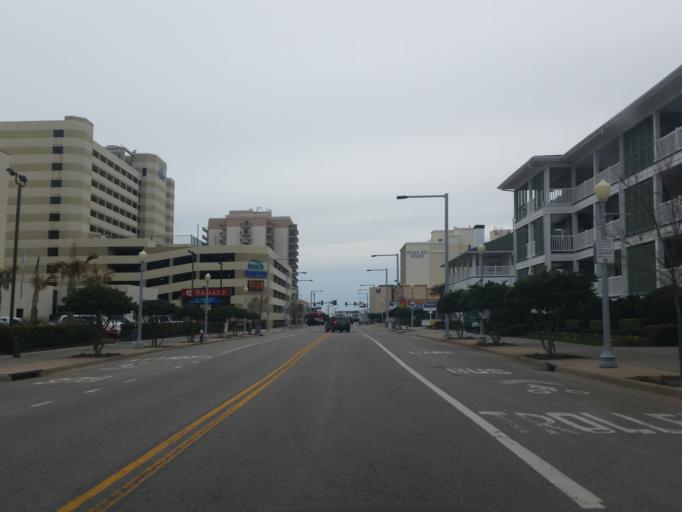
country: US
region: Virginia
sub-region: City of Virginia Beach
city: Virginia Beach
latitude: 36.8357
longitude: -75.9717
